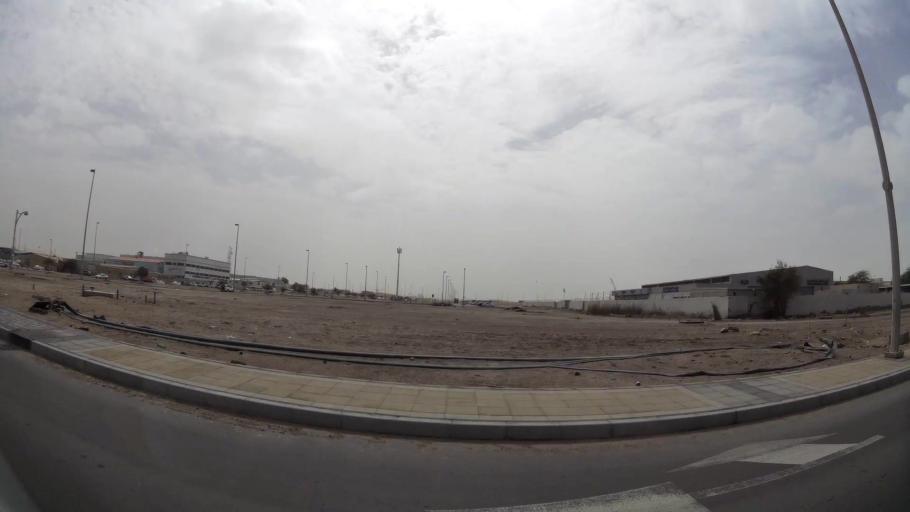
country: AE
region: Abu Dhabi
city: Abu Dhabi
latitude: 24.3721
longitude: 54.4807
